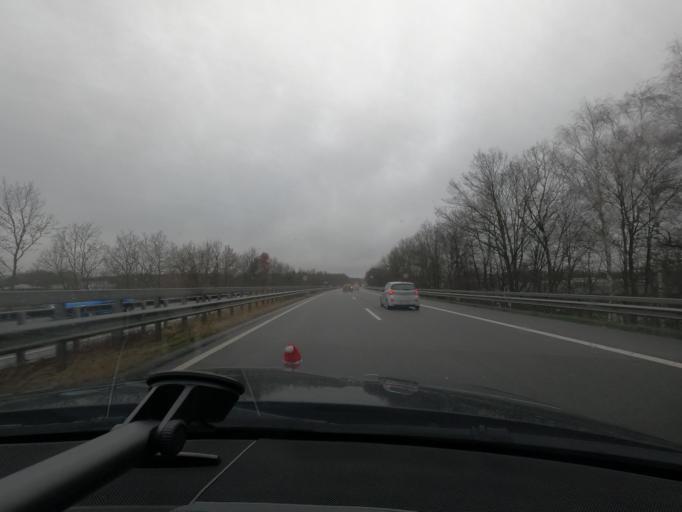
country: DE
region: Lower Saxony
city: Harmstorf
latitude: 53.3833
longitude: 10.0042
